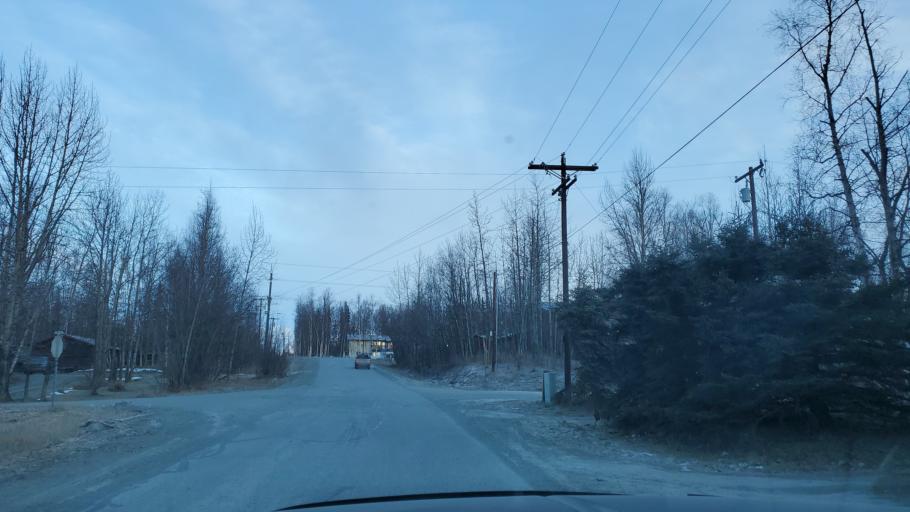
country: US
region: Alaska
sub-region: Matanuska-Susitna Borough
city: Lakes
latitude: 61.6126
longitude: -149.3065
